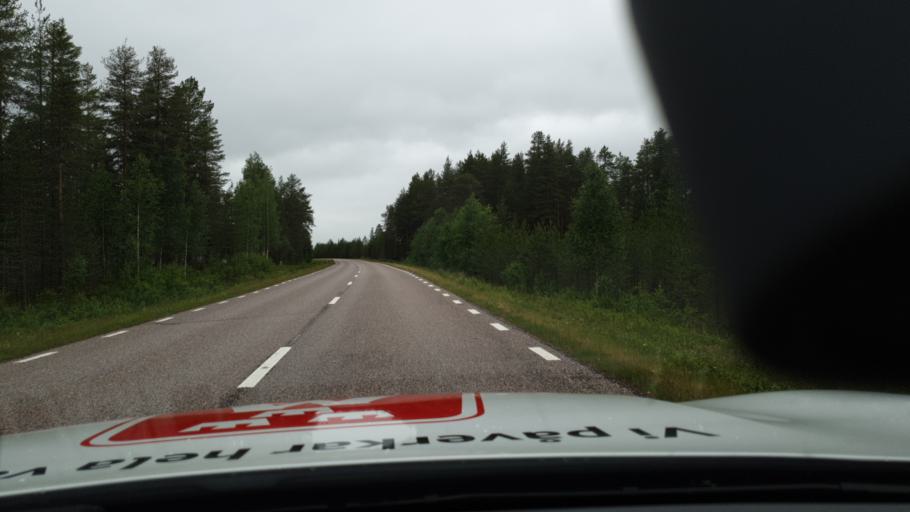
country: FI
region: Lapland
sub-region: Tunturi-Lappi
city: Kolari
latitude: 67.0346
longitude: 23.7102
